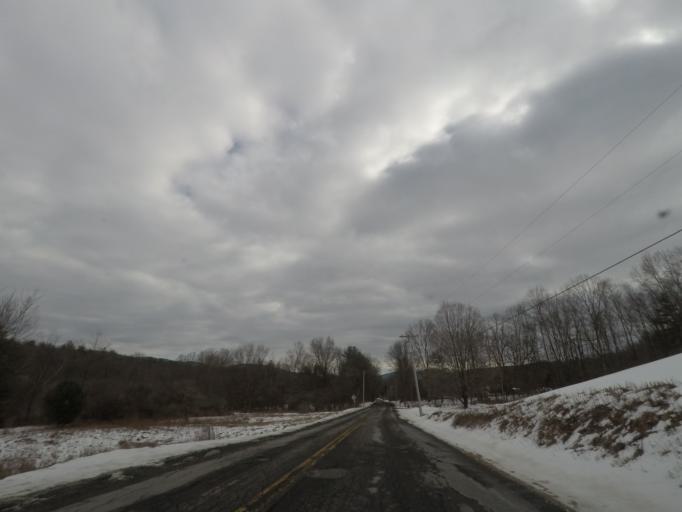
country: US
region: New York
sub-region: Rensselaer County
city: Hoosick Falls
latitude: 42.8592
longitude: -73.3538
